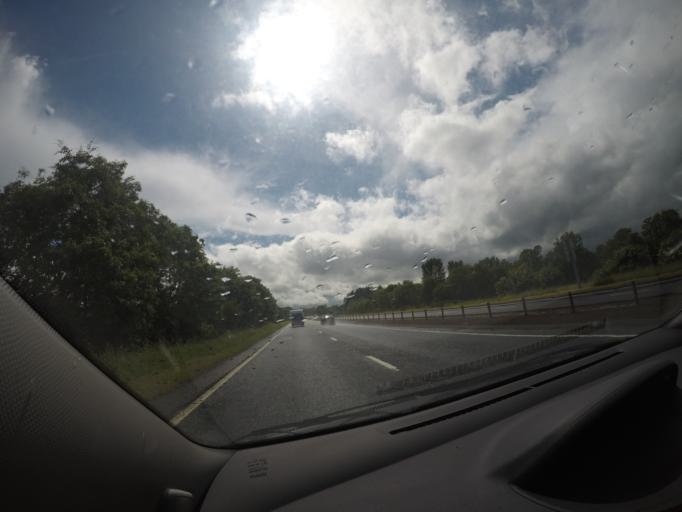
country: GB
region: Scotland
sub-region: Perth and Kinross
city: Auchterarder
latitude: 56.2997
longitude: -3.6783
